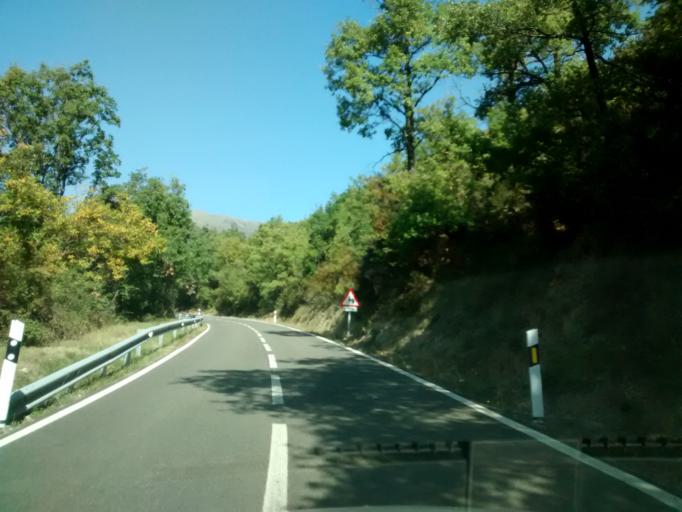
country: ES
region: Aragon
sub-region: Provincia de Huesca
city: Fiscal
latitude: 42.5145
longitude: -0.1262
